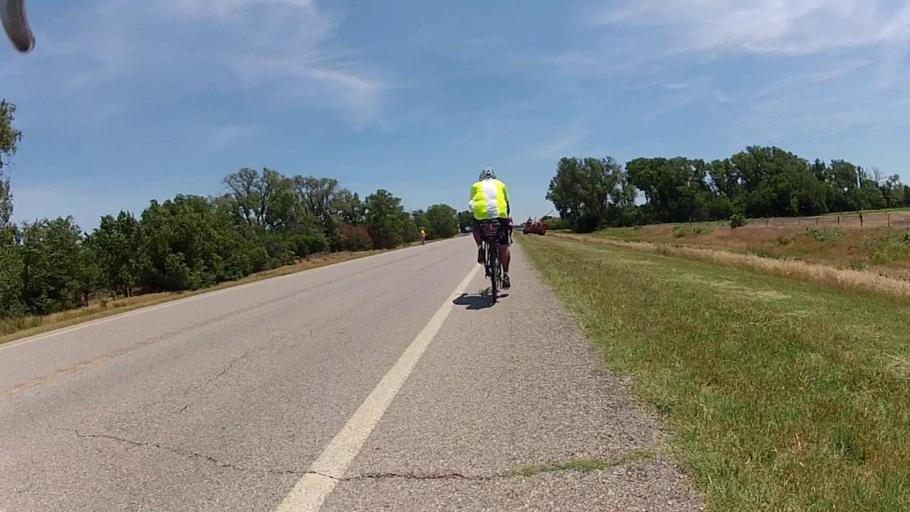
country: US
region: Kansas
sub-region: Barber County
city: Medicine Lodge
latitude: 37.2534
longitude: -98.4549
